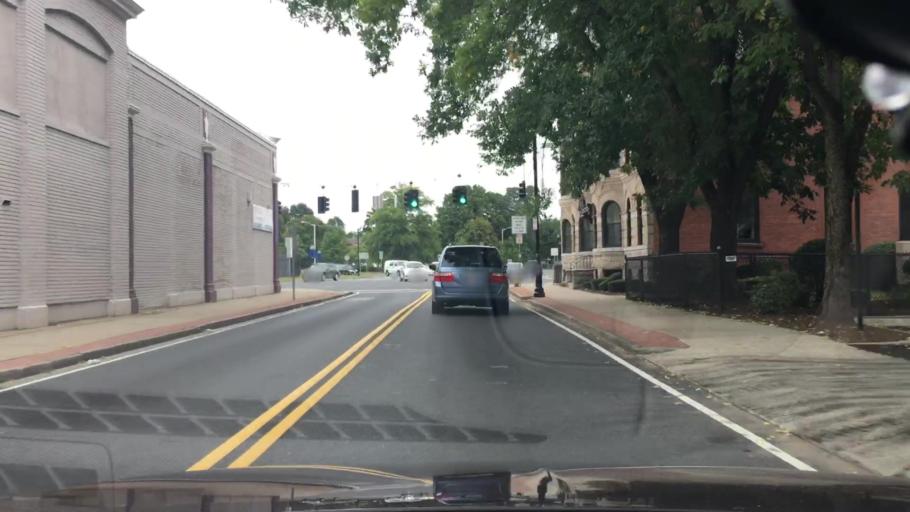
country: US
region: Massachusetts
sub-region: Hampden County
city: Springfield
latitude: 42.1088
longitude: -72.5741
